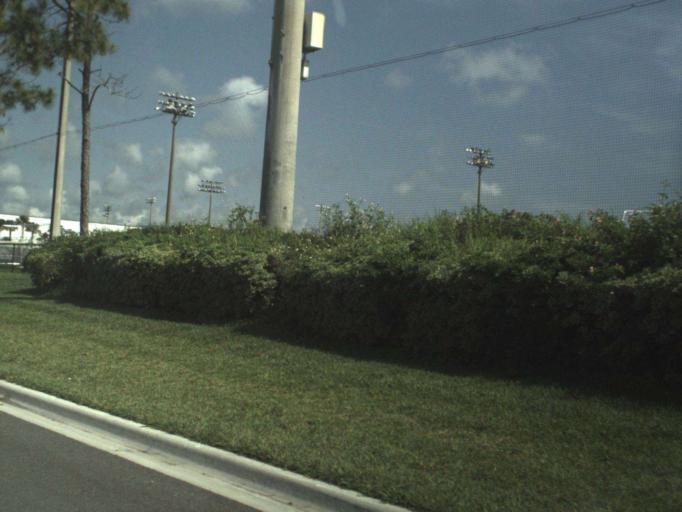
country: US
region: Florida
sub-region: Volusia County
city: Daytona Beach
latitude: 29.1889
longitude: -81.0448
